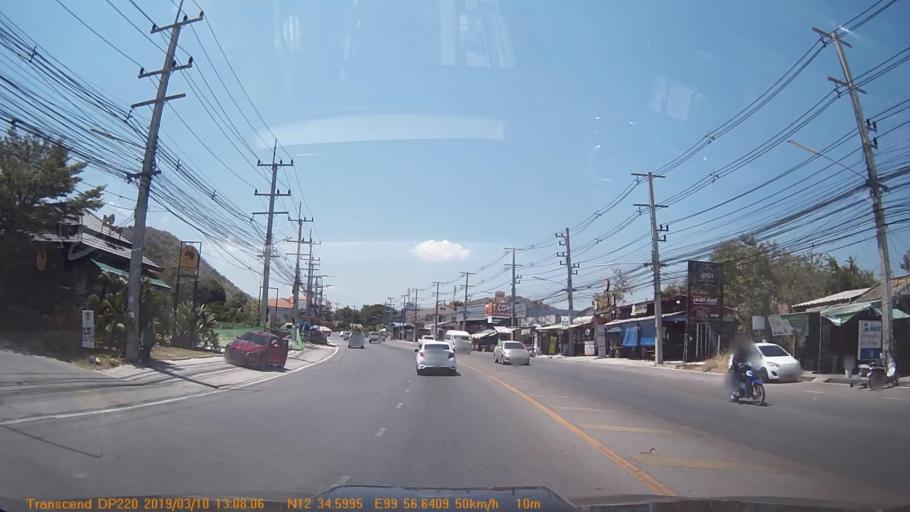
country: TH
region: Prachuap Khiri Khan
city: Hua Hin
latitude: 12.5766
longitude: 99.9442
